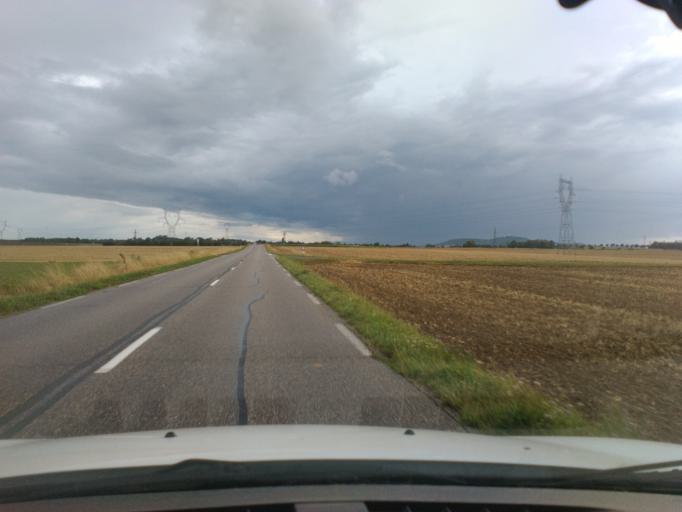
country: FR
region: Lorraine
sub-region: Departement de Meurthe-et-Moselle
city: Vezelise
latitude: 48.4846
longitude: 6.1432
